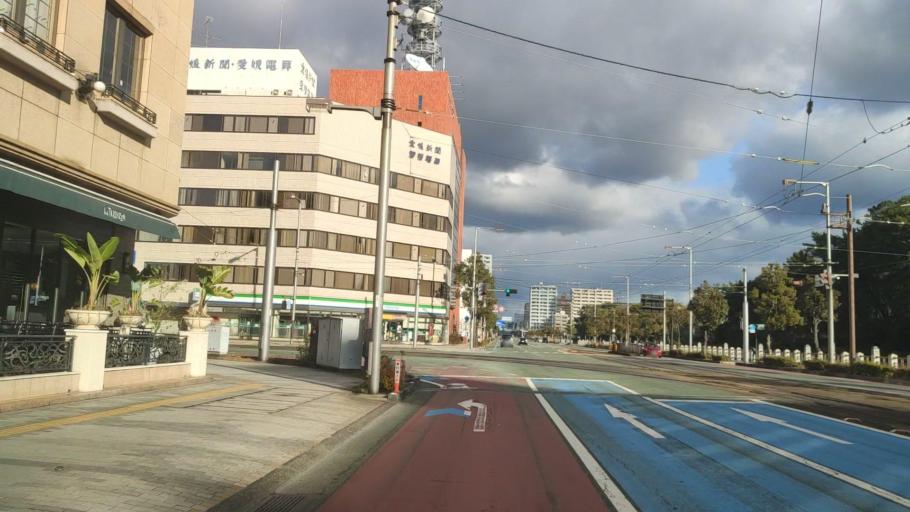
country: JP
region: Ehime
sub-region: Shikoku-chuo Shi
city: Matsuyama
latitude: 33.8397
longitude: 132.7586
